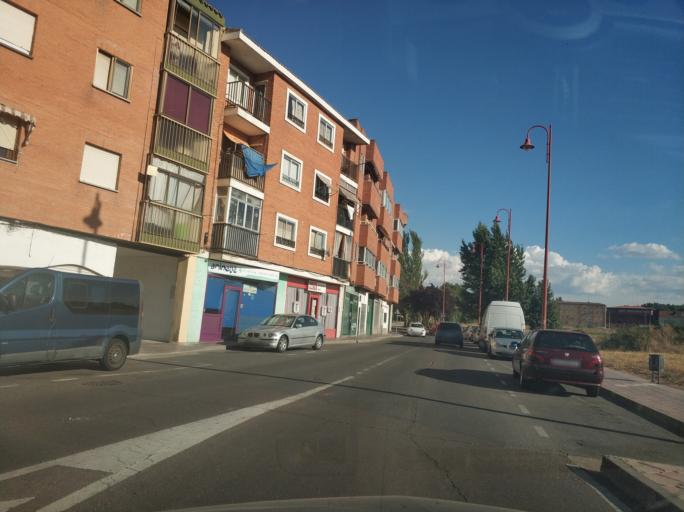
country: ES
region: Castille and Leon
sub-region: Provincia de Salamanca
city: Santa Marta de Tormes
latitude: 40.9499
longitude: -5.6335
